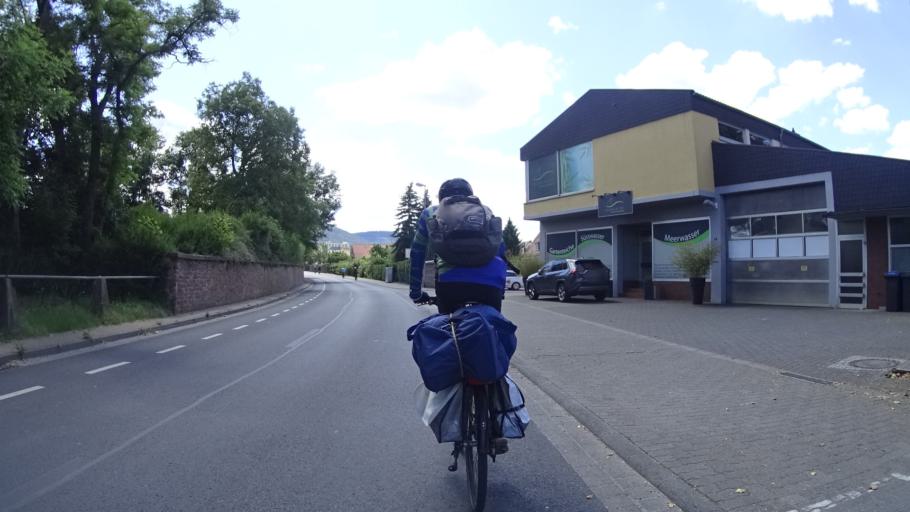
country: DE
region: Bavaria
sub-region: Regierungsbezirk Unterfranken
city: Kleinheubach
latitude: 49.7193
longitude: 9.2160
